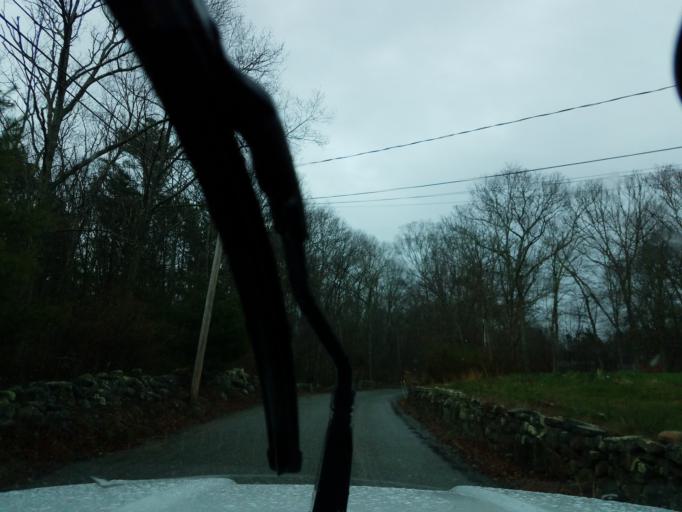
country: US
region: Rhode Island
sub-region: Washington County
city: Ashaway
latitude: 41.4458
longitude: -71.8211
